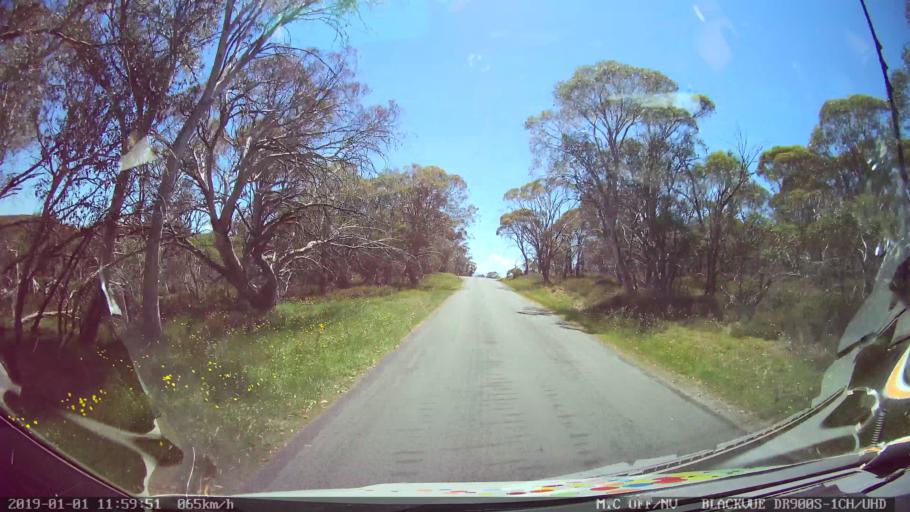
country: AU
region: New South Wales
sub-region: Snowy River
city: Jindabyne
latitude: -35.8890
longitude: 148.4550
